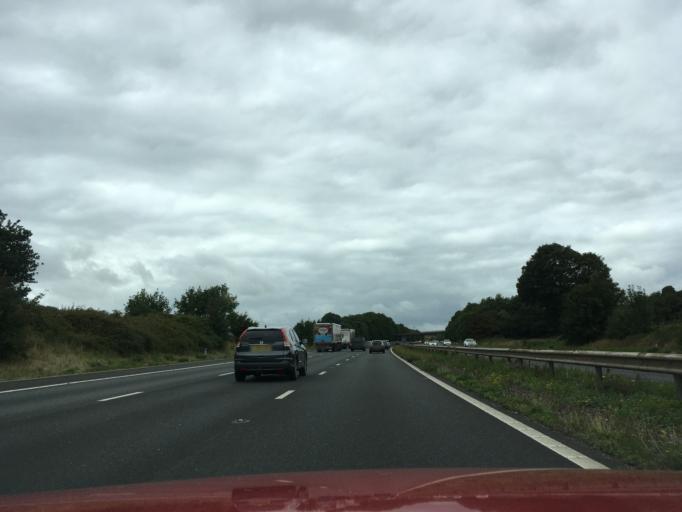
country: GB
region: England
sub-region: Somerset
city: Taunton
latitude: 50.9801
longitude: -3.1207
